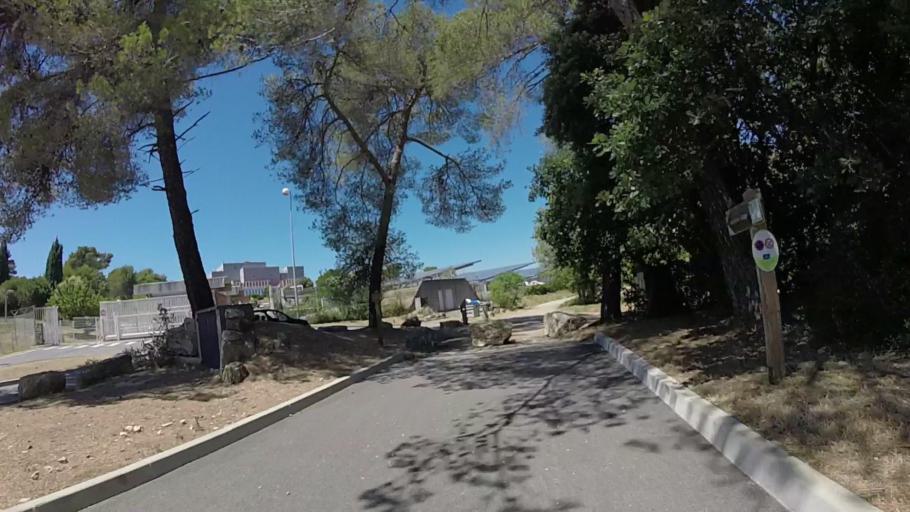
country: FR
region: Provence-Alpes-Cote d'Azur
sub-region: Departement des Alpes-Maritimes
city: Valbonne
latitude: 43.6283
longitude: 7.0358
